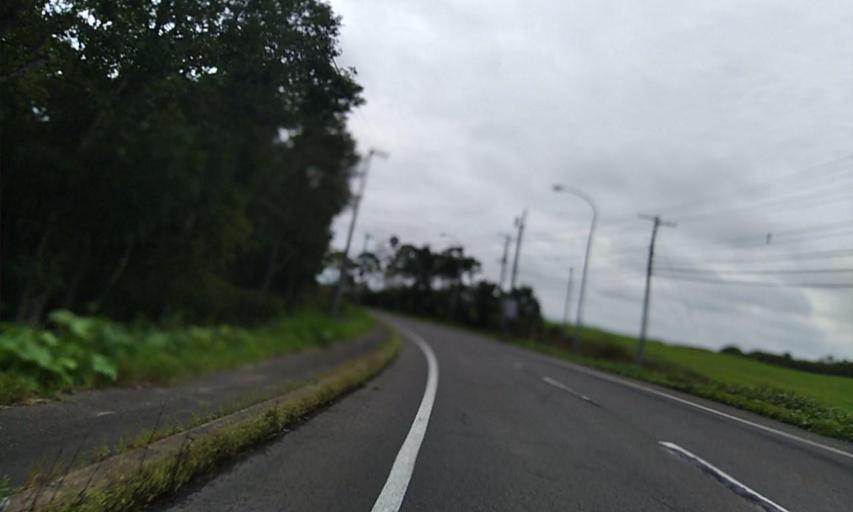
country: JP
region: Hokkaido
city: Shibetsu
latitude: 43.5820
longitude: 145.2112
